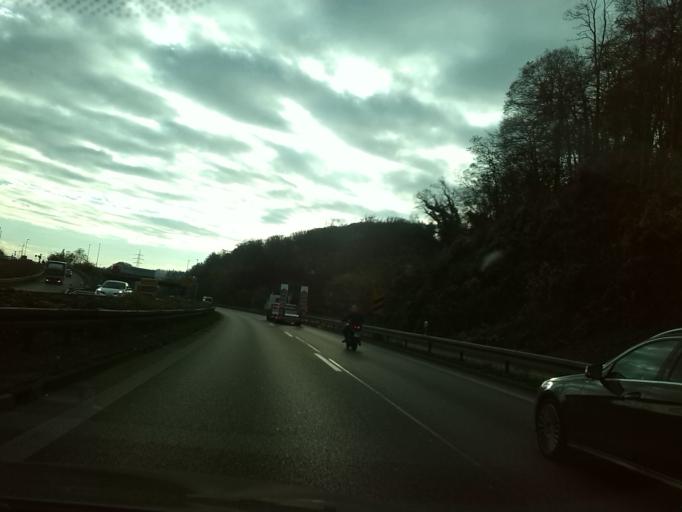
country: DE
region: Baden-Wuerttemberg
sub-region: Regierungsbezirk Stuttgart
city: Esslingen
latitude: 48.7287
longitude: 9.3168
